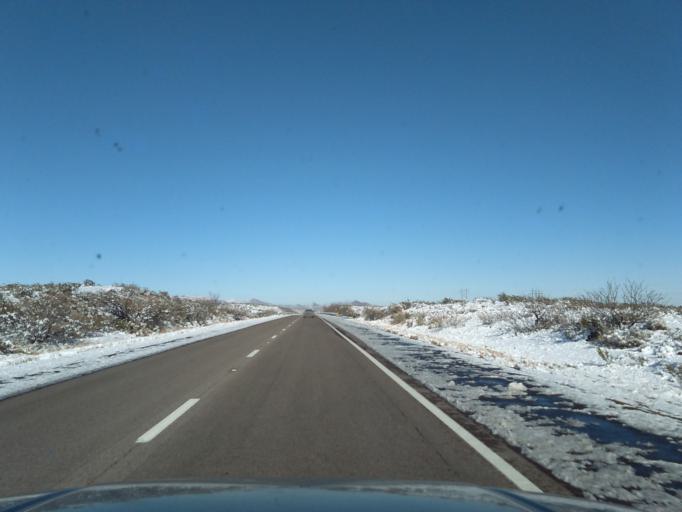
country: US
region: New Mexico
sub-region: Socorro County
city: Socorro
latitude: 33.6769
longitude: -107.0744
